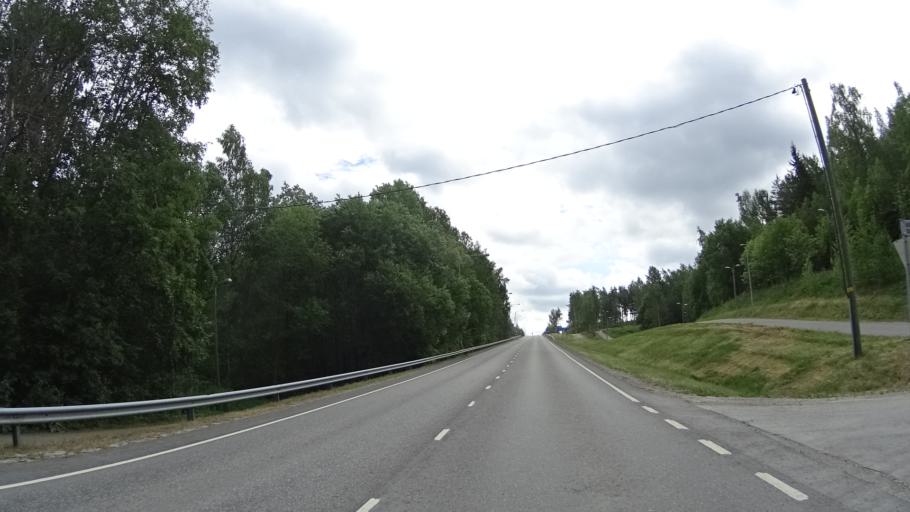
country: FI
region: Uusimaa
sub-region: Helsinki
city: Kirkkonummi
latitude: 60.2716
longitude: 24.4329
